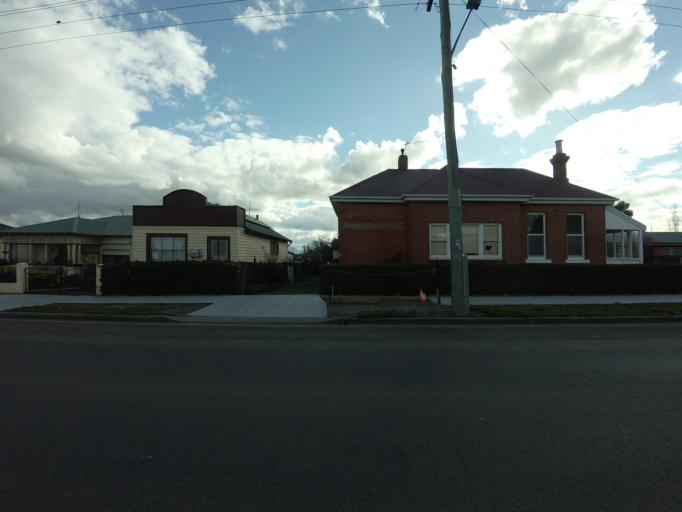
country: AU
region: Tasmania
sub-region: Northern Midlands
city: Longford
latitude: -41.6866
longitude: 147.0802
